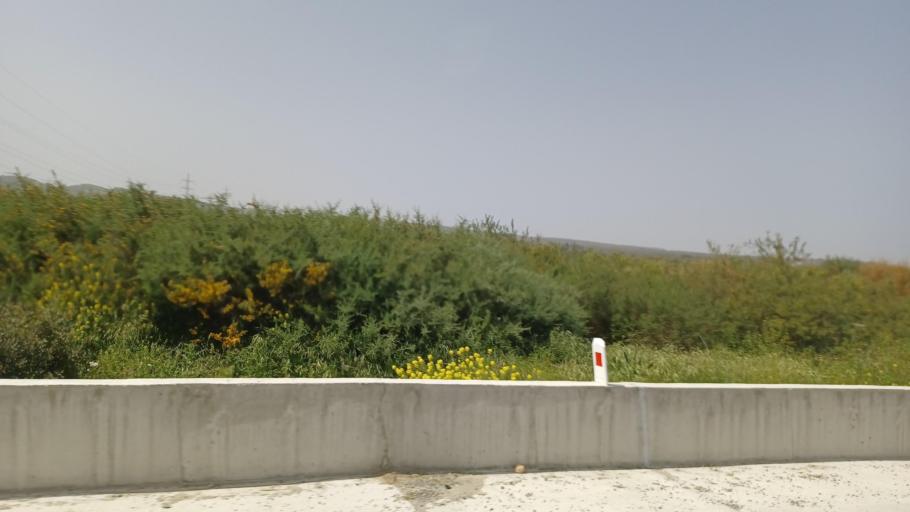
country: CY
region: Limassol
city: Pissouri
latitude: 34.7093
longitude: 32.7440
